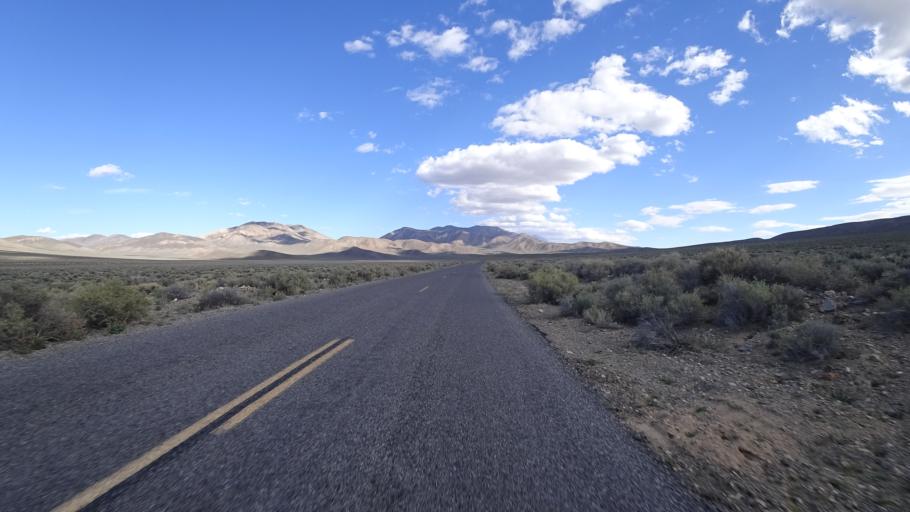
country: US
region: Nevada
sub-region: Nye County
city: Beatty
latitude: 36.3769
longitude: -117.1426
